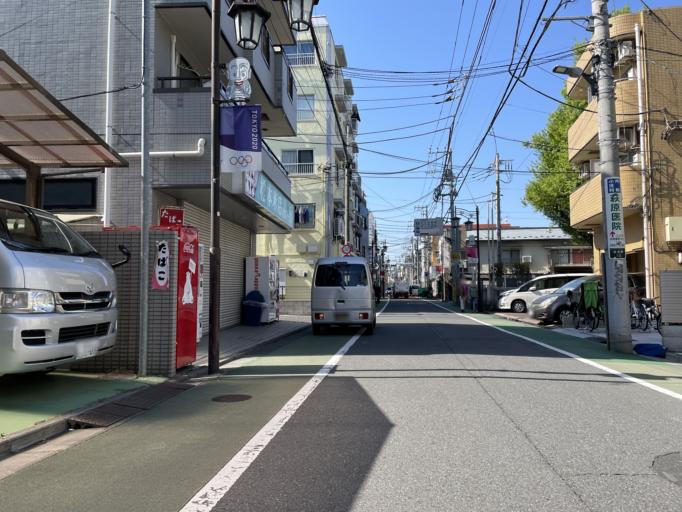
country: JP
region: Saitama
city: Kawaguchi
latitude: 35.7525
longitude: 139.6941
